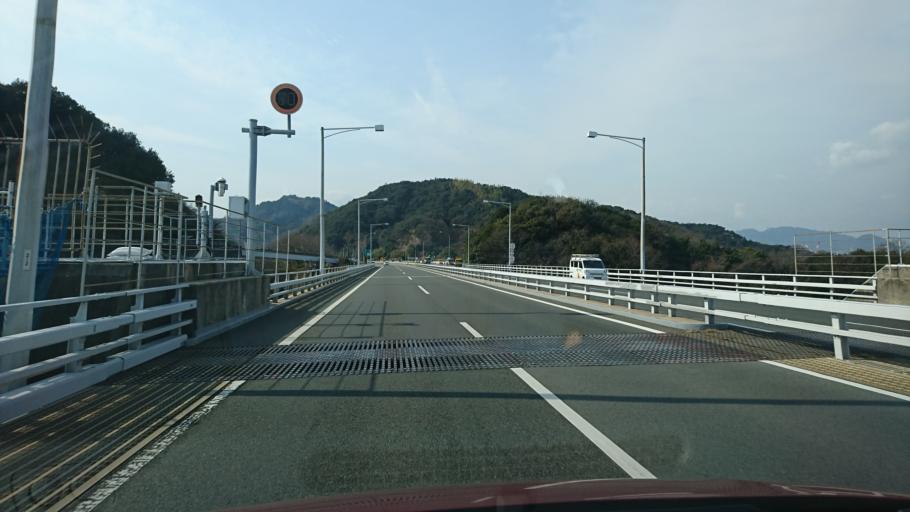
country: JP
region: Hiroshima
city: Onomichi
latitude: 34.3546
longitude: 133.1743
